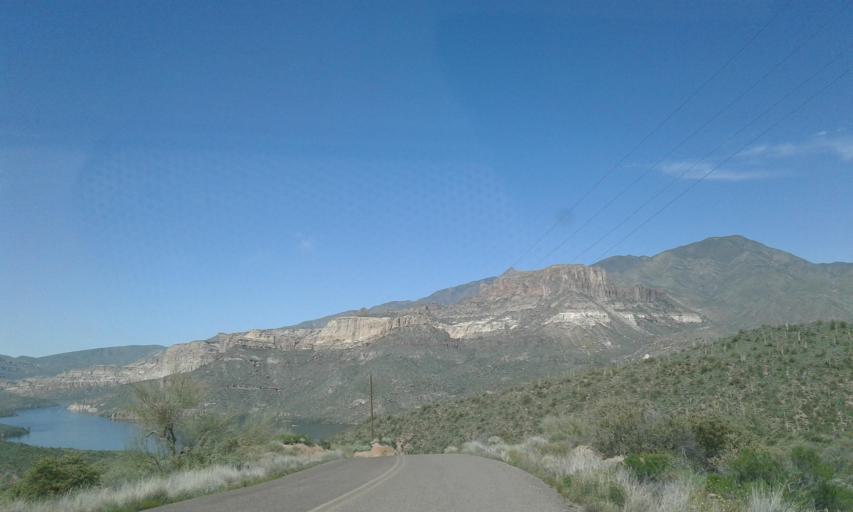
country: US
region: Arizona
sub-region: Gila County
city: Tonto Basin
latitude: 33.5670
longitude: -111.2449
